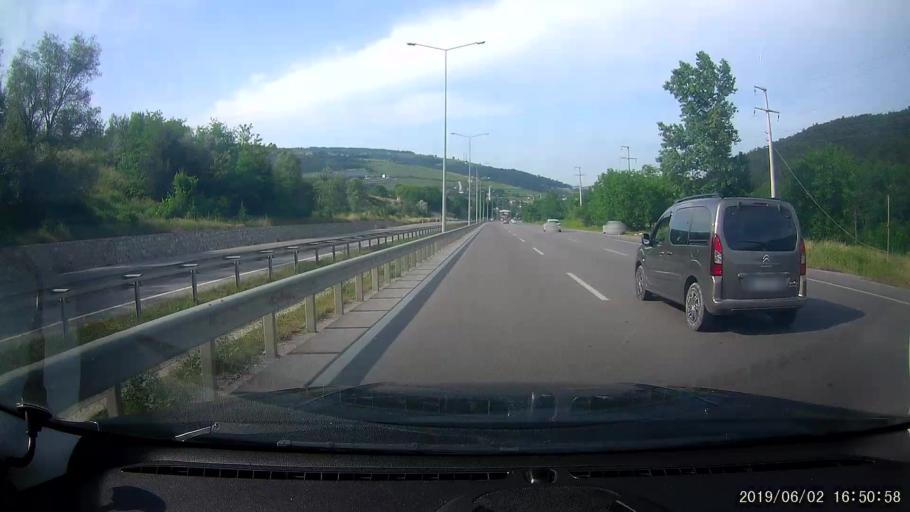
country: TR
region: Samsun
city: Taflan
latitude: 41.2660
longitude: 36.1770
